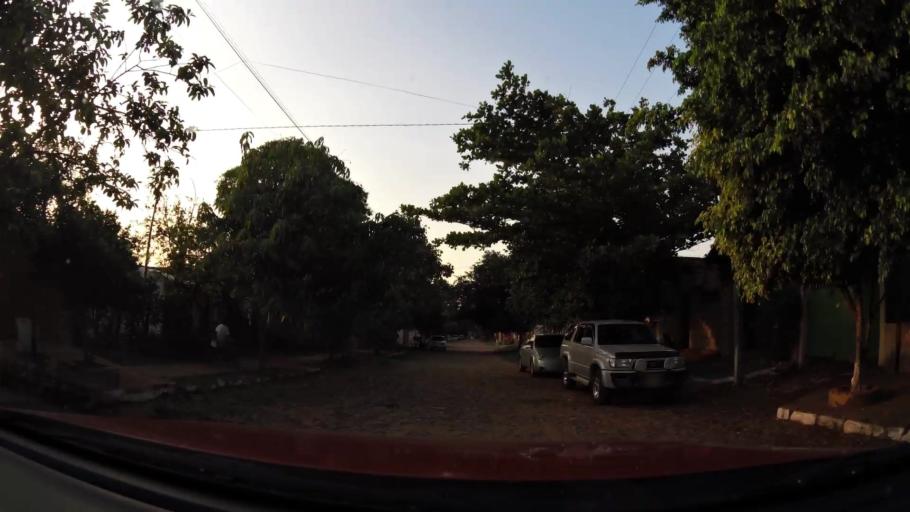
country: PY
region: Central
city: Lambare
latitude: -25.3466
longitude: -57.6000
